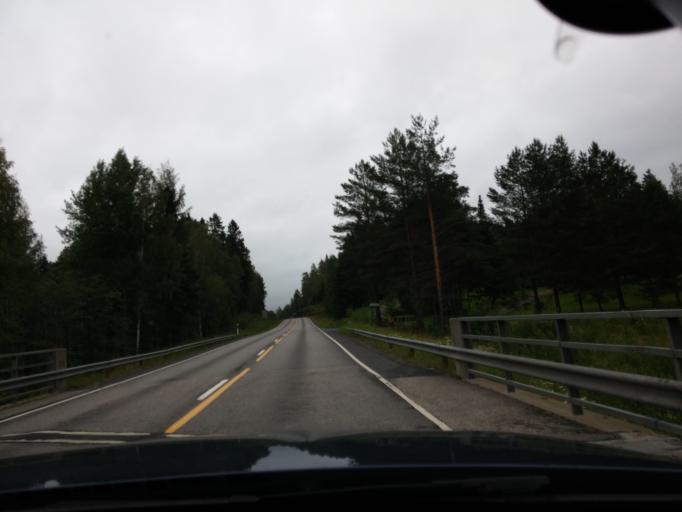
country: FI
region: Central Finland
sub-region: Saarijaervi-Viitasaari
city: Saarijaervi
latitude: 62.6883
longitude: 25.2654
